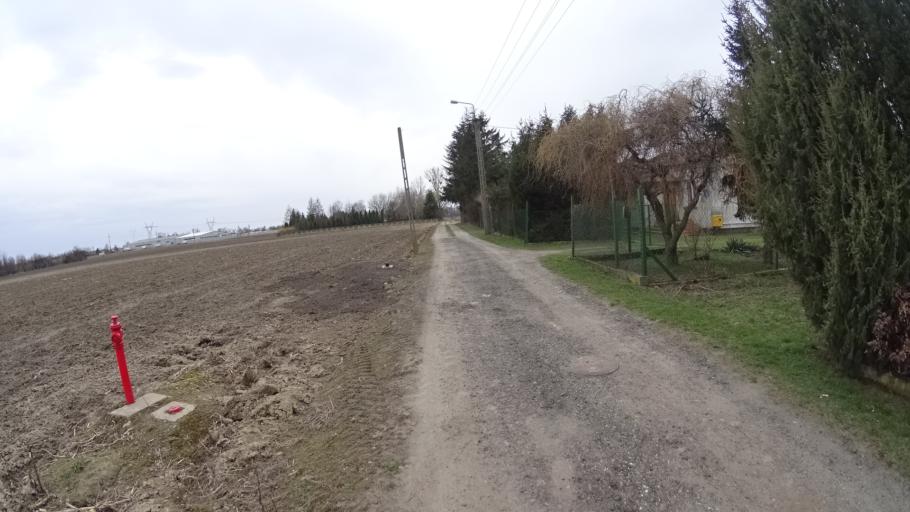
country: PL
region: Masovian Voivodeship
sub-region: Powiat warszawski zachodni
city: Stare Babice
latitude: 52.2431
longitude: 20.8130
